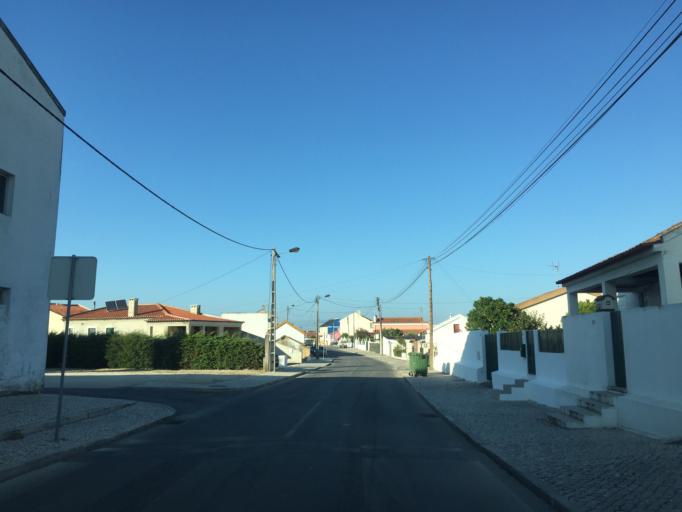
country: PT
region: Lisbon
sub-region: Azambuja
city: Aveiras de Cima
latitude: 39.1354
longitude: -8.9242
